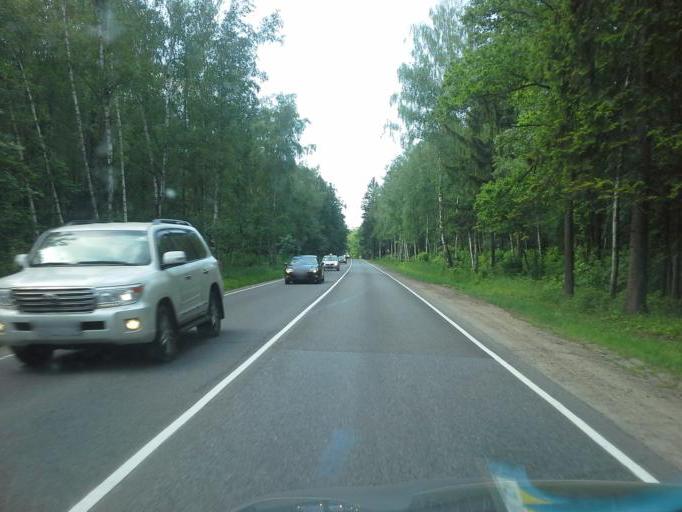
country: RU
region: Moskovskaya
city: Gorki Vtoryye
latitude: 55.7075
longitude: 37.2216
